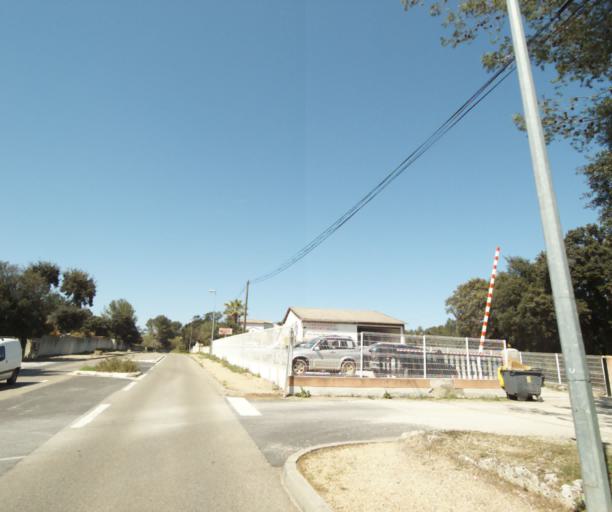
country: FR
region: Languedoc-Roussillon
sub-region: Departement de l'Herault
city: Sussargues
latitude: 43.7055
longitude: 4.0062
